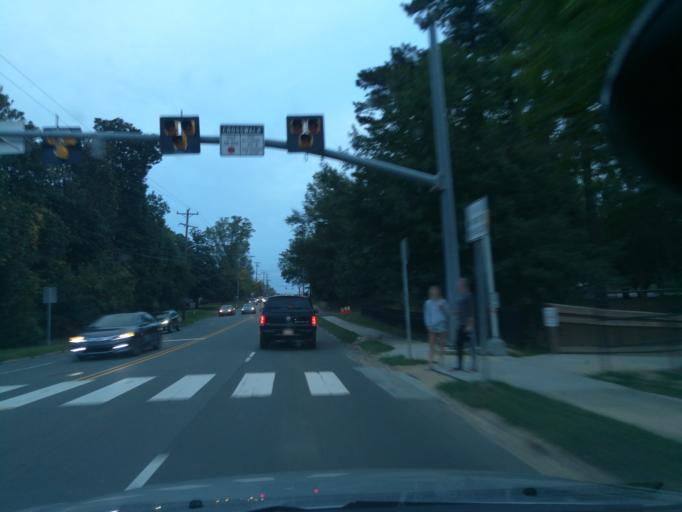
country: US
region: North Carolina
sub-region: Durham County
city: Durham
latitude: 36.0255
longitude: -78.9215
